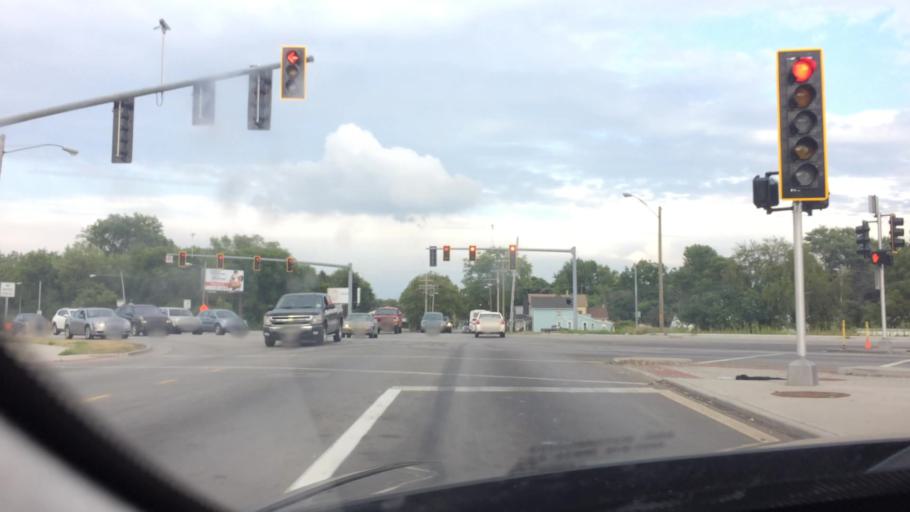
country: US
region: Ohio
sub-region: Wood County
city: Rossford
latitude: 41.6308
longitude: -83.5676
